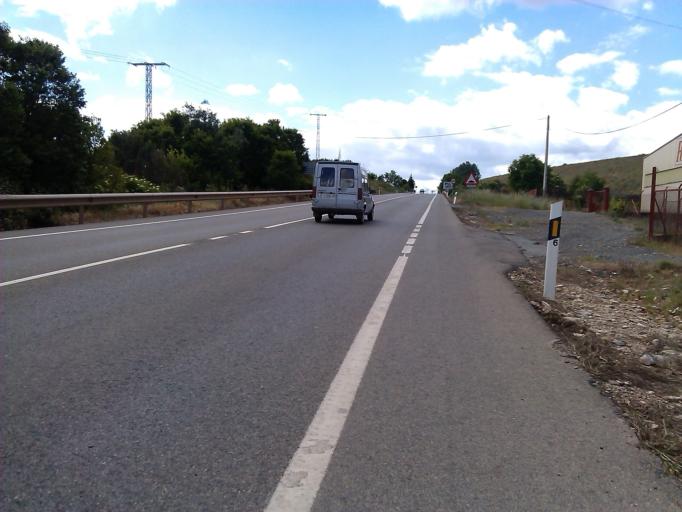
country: ES
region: La Rioja
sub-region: Provincia de La Rioja
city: Najera
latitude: 42.4253
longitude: -2.7392
